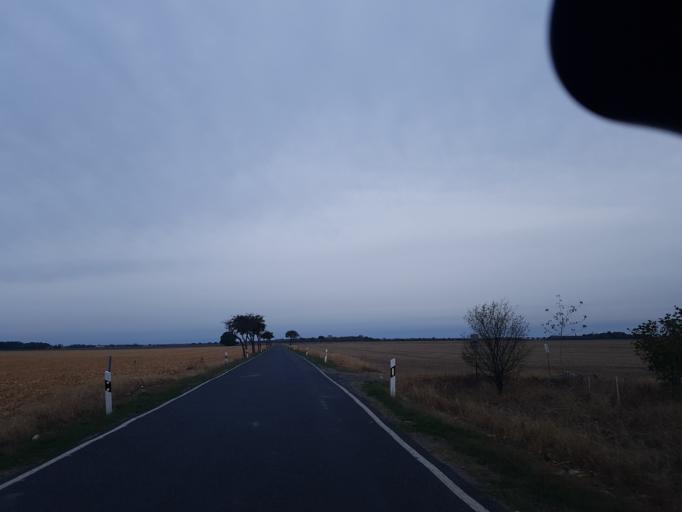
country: DE
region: Saxony
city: Belgern
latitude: 51.4980
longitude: 13.1775
